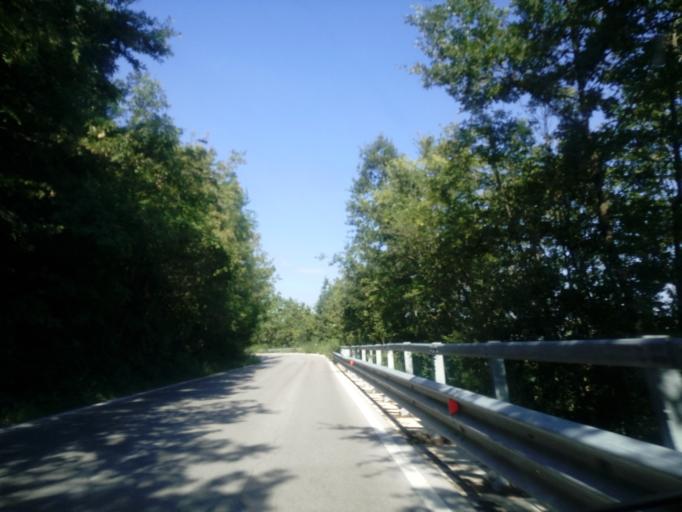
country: IT
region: Molise
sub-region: Provincia di Campobasso
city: Gildone
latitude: 41.5151
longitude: 14.7473
